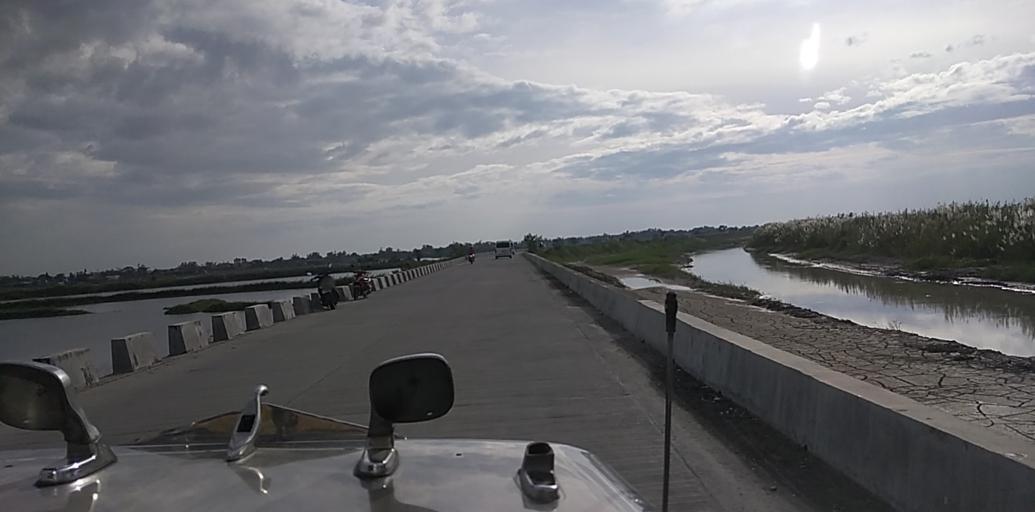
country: PH
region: Central Luzon
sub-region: Province of Pampanga
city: Minalin
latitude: 14.9722
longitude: 120.6787
